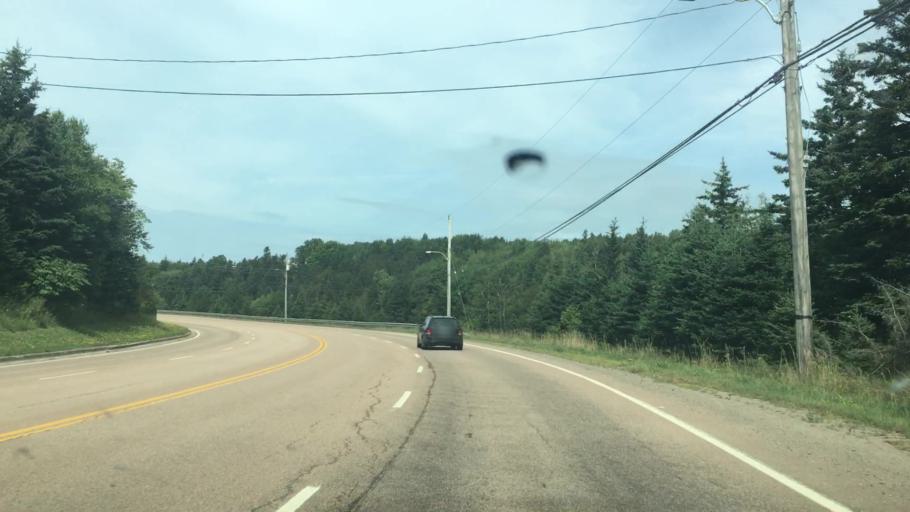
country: CA
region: Nova Scotia
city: Port Hawkesbury
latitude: 45.6242
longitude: -61.3655
